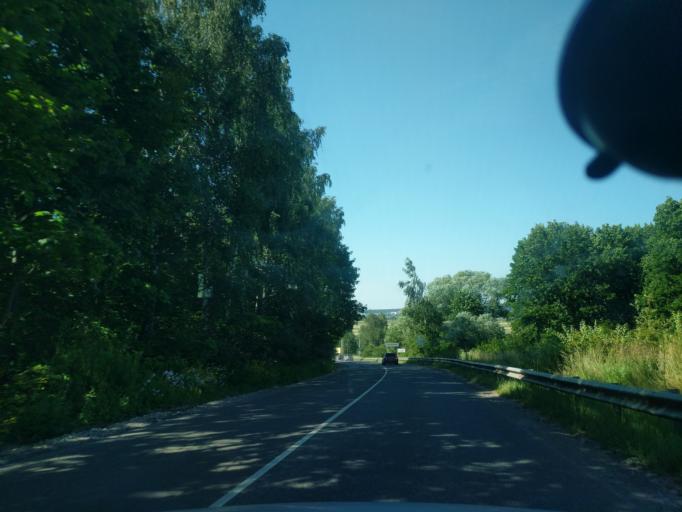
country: RU
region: Moskovskaya
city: Serpukhov
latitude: 54.8584
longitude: 37.4767
